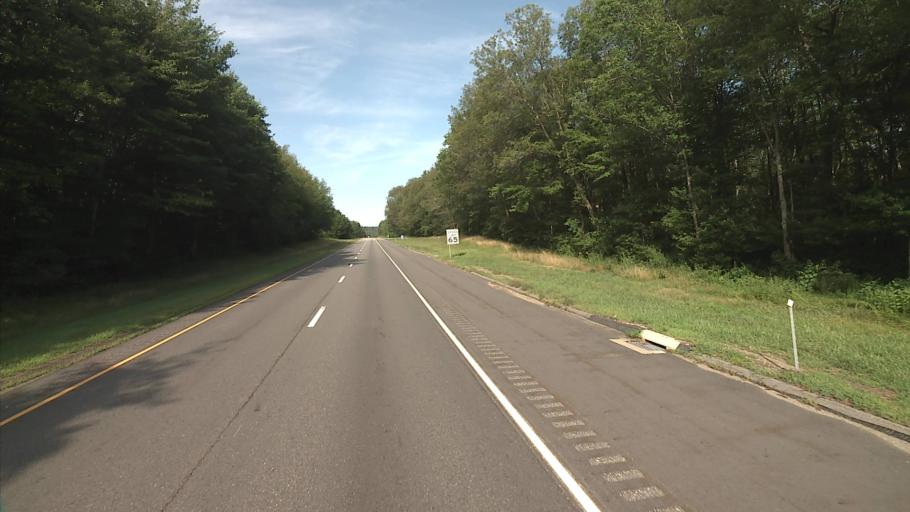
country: US
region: Connecticut
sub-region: New London County
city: Colchester
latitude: 41.5685
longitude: -72.2230
